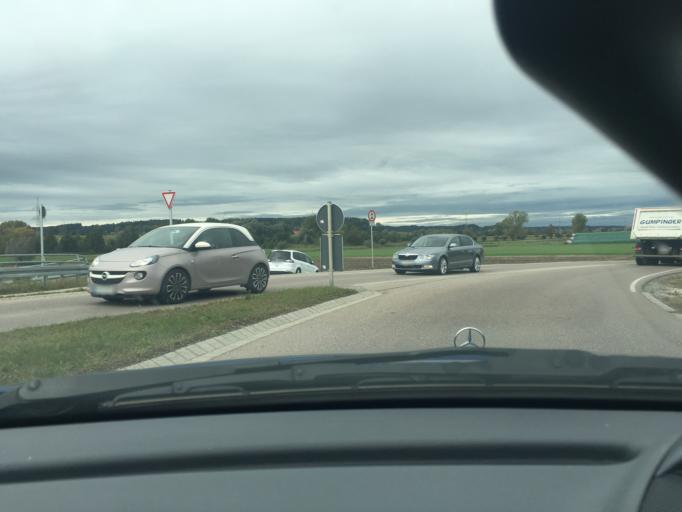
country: DE
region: Bavaria
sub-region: Swabia
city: Gablingen
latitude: 48.4202
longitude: 10.8259
